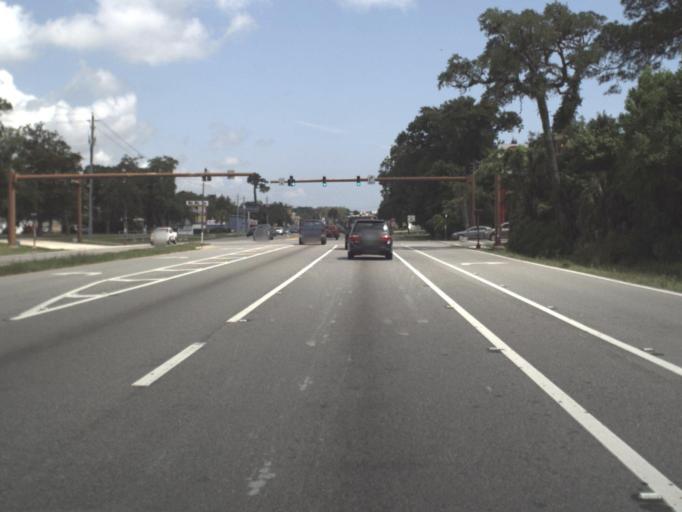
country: US
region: Florida
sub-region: Saint Johns County
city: Saint Augustine
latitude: 29.8746
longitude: -81.3236
